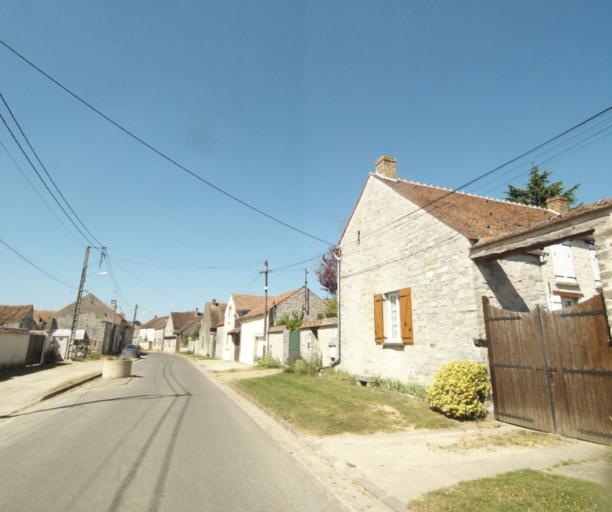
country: FR
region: Ile-de-France
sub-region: Departement de Seine-et-Marne
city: Acheres-la-Foret
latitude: 48.3437
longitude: 2.5647
